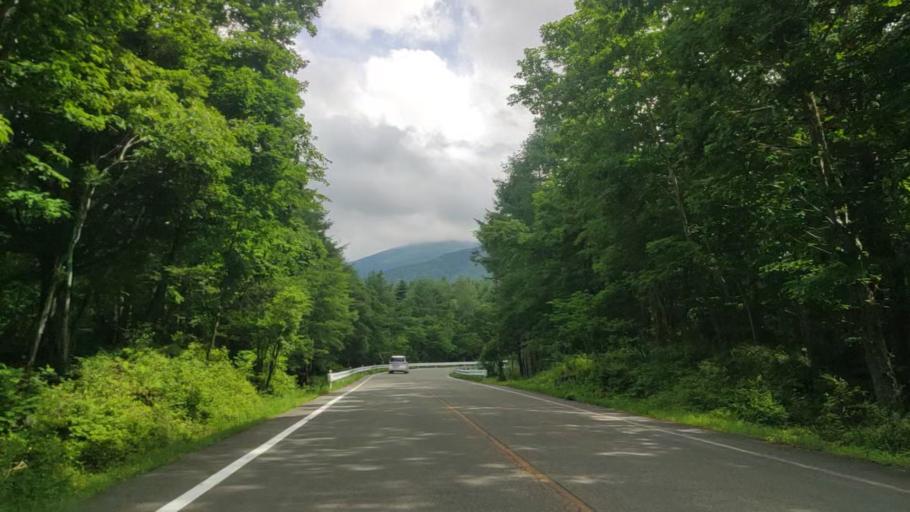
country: JP
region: Yamanashi
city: Fujikawaguchiko
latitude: 35.4277
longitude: 138.7395
